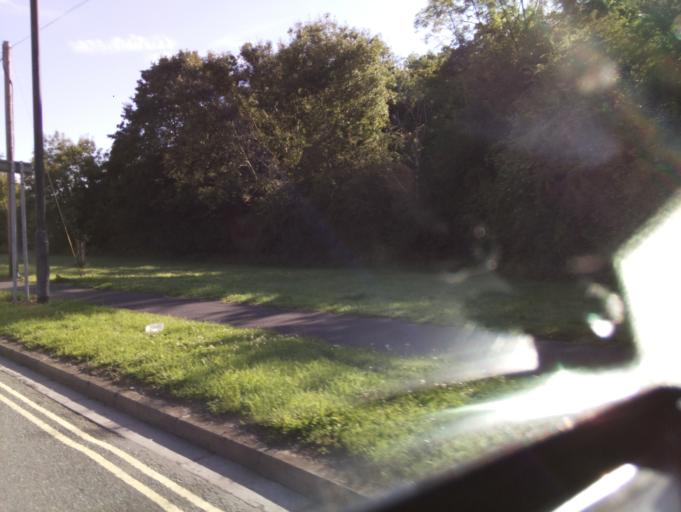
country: GB
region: England
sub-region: Bath and North East Somerset
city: Whitchurch
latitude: 51.4180
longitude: -2.5539
